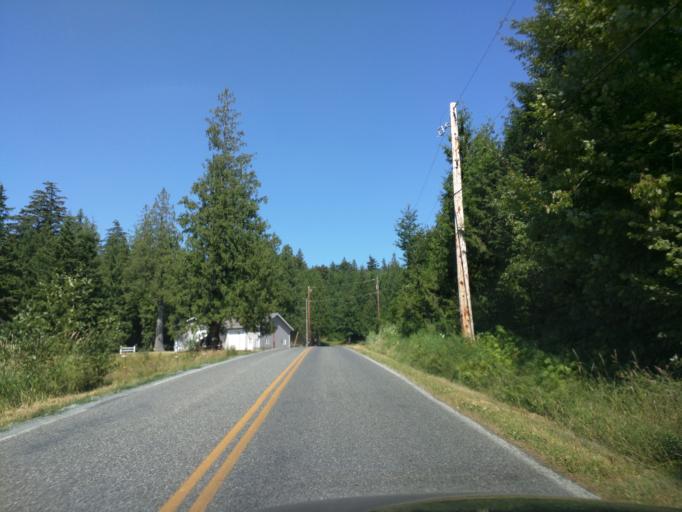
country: US
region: Washington
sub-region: Whatcom County
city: Nooksack
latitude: 48.9314
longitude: -122.2596
